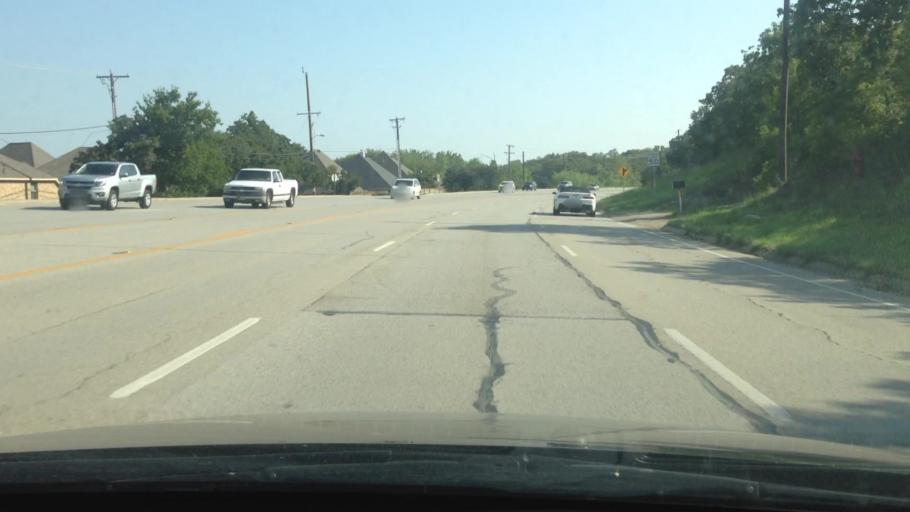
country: US
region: Texas
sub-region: Tarrant County
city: Colleyville
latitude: 32.8797
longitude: -97.2036
